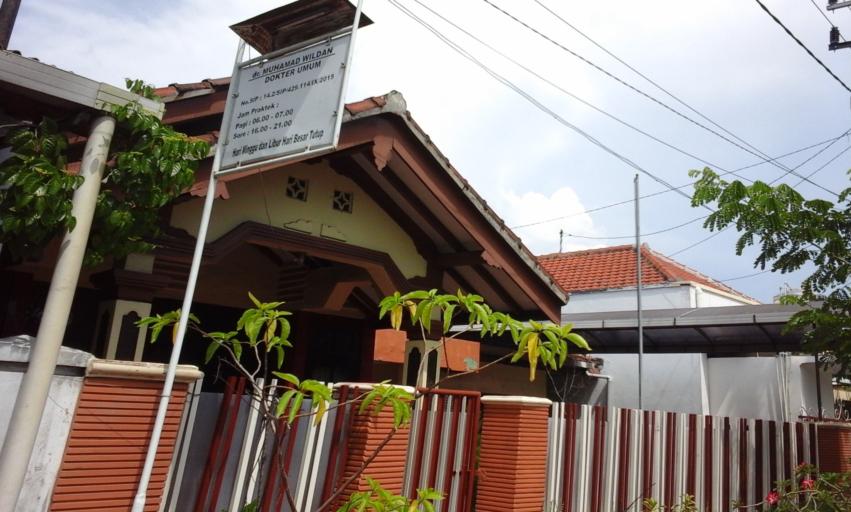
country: ID
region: East Java
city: Banyuwangi
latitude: -8.2348
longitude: 114.3573
